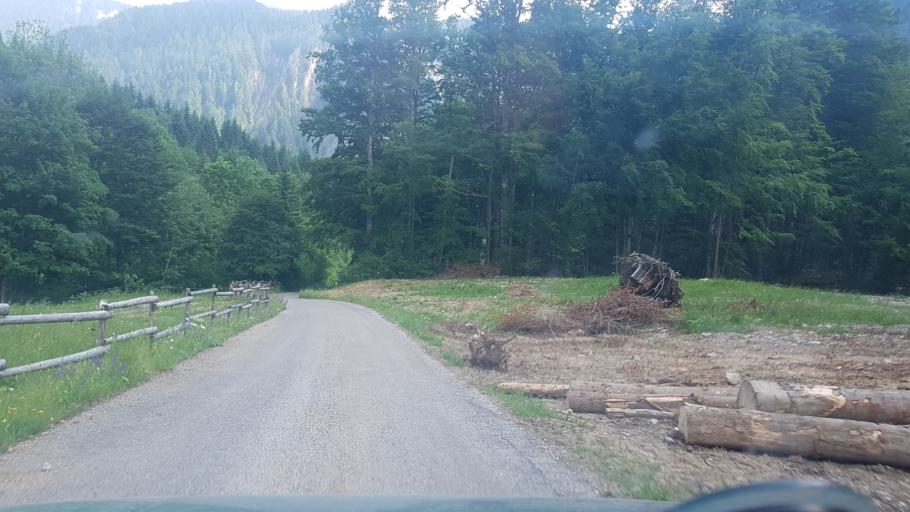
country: IT
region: Friuli Venezia Giulia
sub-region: Provincia di Udine
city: Paularo
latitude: 46.5322
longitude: 13.2101
